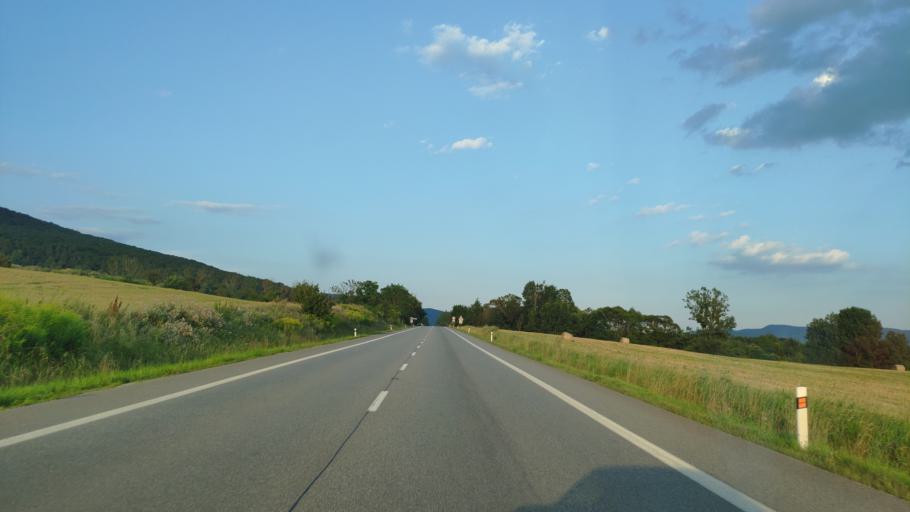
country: SK
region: Kosicky
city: Roznava
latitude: 48.6514
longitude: 20.5535
